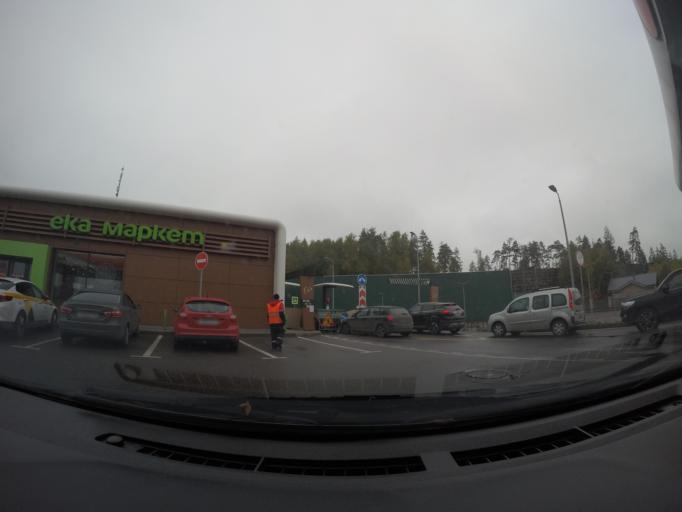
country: RU
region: Moskovskaya
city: Petrovo-Dal'neye
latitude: 55.7782
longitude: 37.1863
